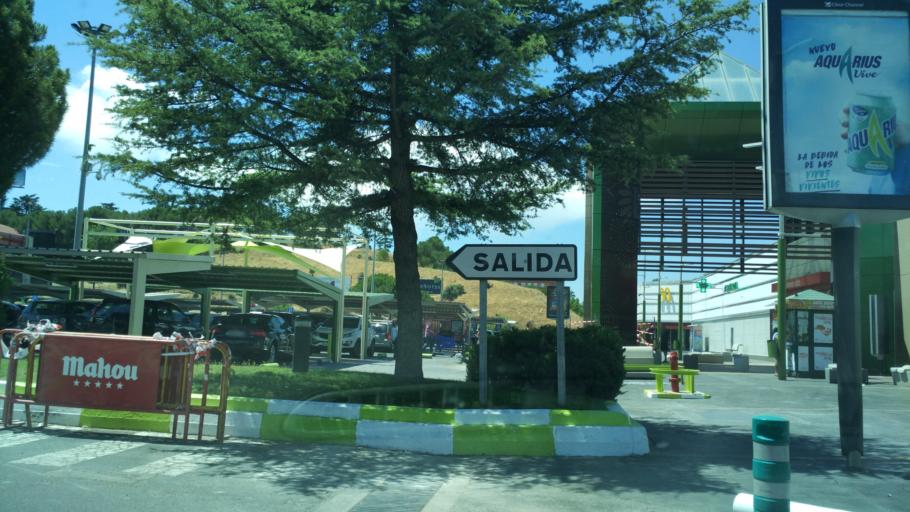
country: ES
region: Madrid
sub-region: Provincia de Madrid
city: Alcobendas
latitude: 40.5266
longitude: -3.6511
